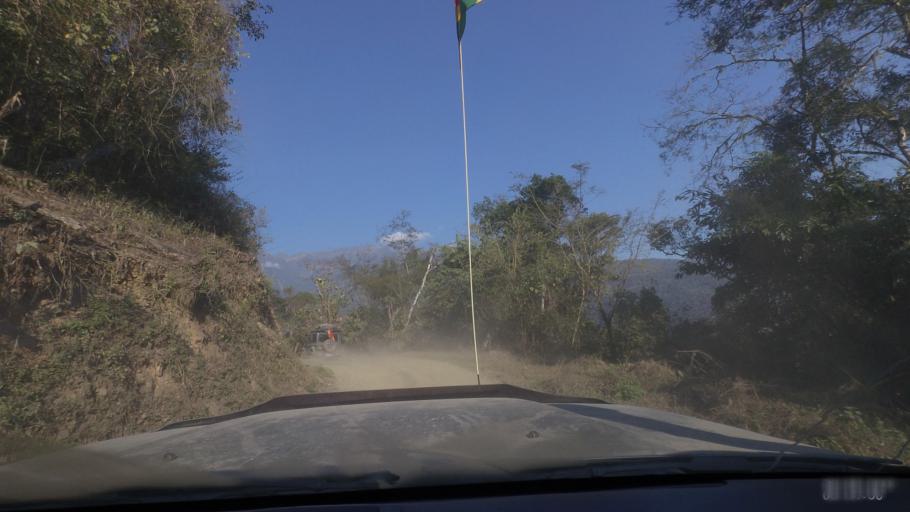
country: BO
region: La Paz
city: Quime
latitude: -16.5142
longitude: -66.7655
